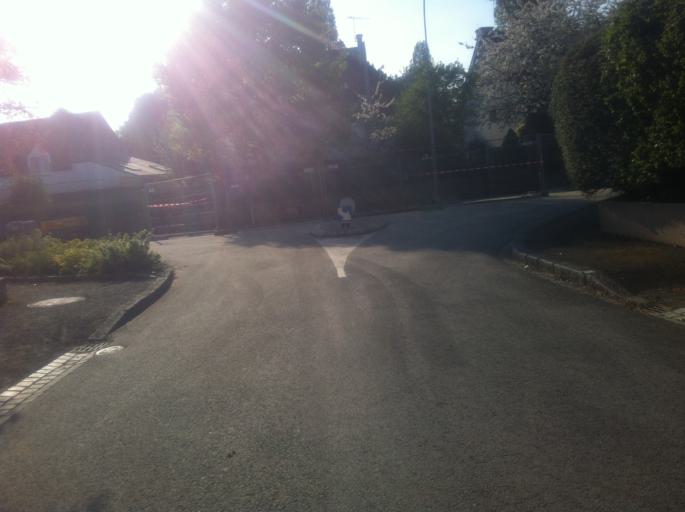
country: FR
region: Brittany
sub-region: Departement d'Ille-et-Vilaine
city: Bruz
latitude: 48.0209
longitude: -1.7355
